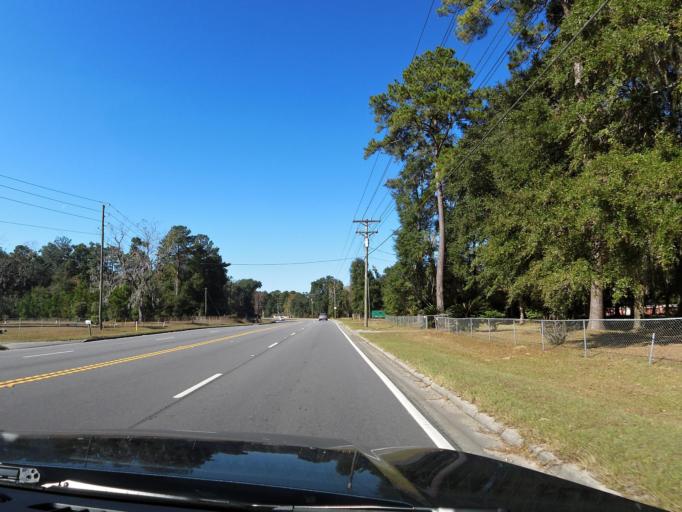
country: US
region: Georgia
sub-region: Liberty County
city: Midway
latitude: 31.7976
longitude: -81.4085
